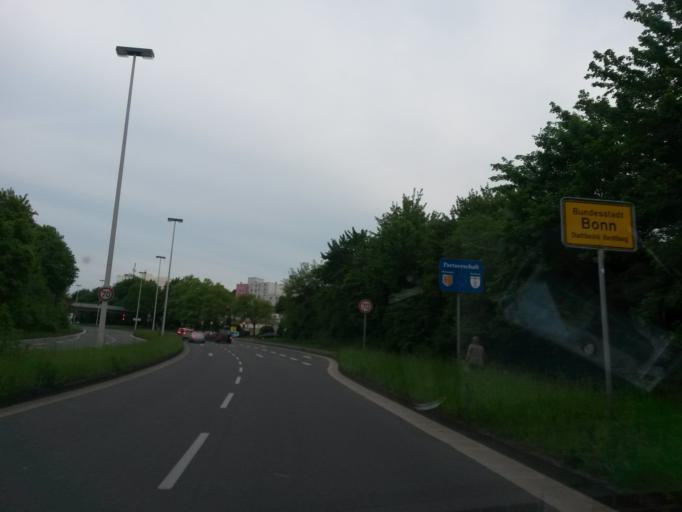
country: DE
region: North Rhine-Westphalia
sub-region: Regierungsbezirk Koln
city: Alfter
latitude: 50.7132
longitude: 7.0293
